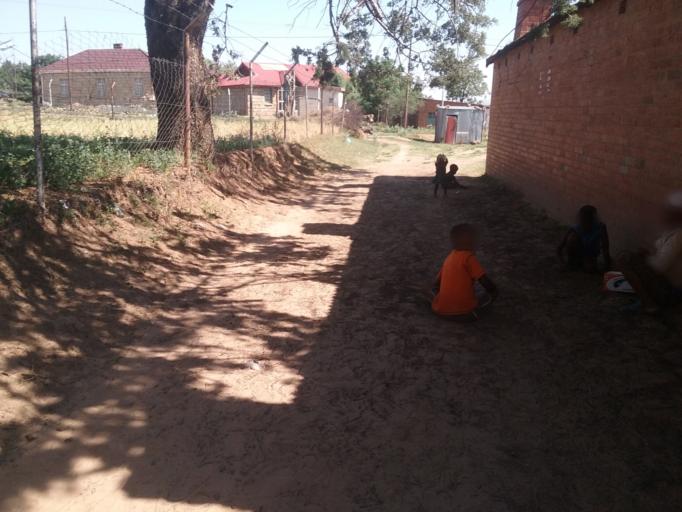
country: LS
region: Berea
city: Teyateyaneng
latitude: -29.1456
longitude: 27.7415
